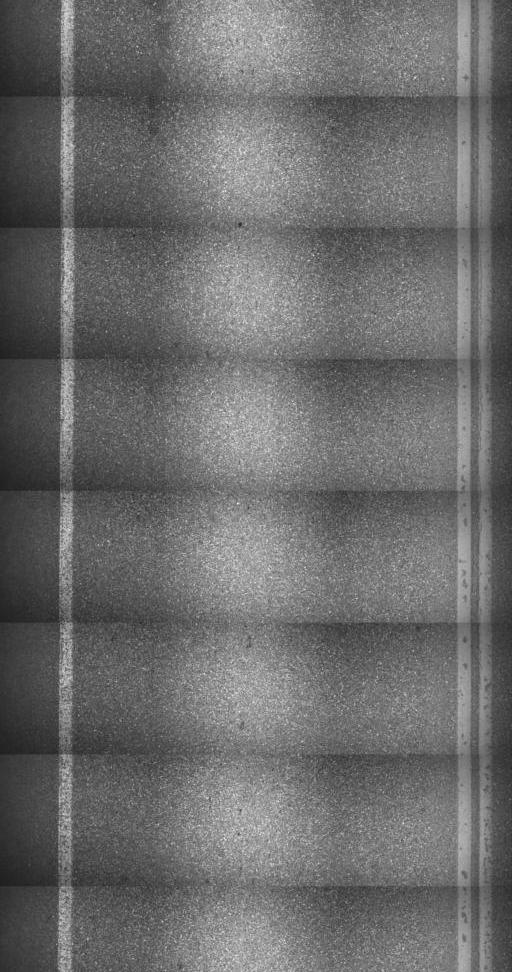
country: US
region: Vermont
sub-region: Lamoille County
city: Johnson
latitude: 44.6221
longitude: -72.6697
